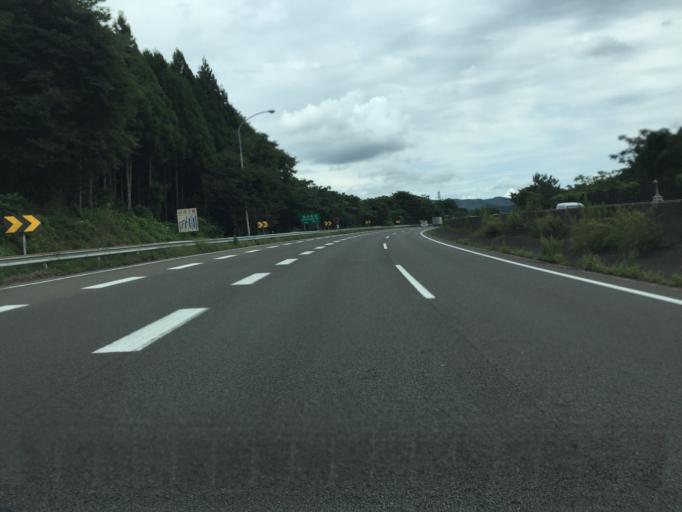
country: JP
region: Fukushima
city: Yanagawamachi-saiwaicho
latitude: 37.9105
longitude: 140.5822
